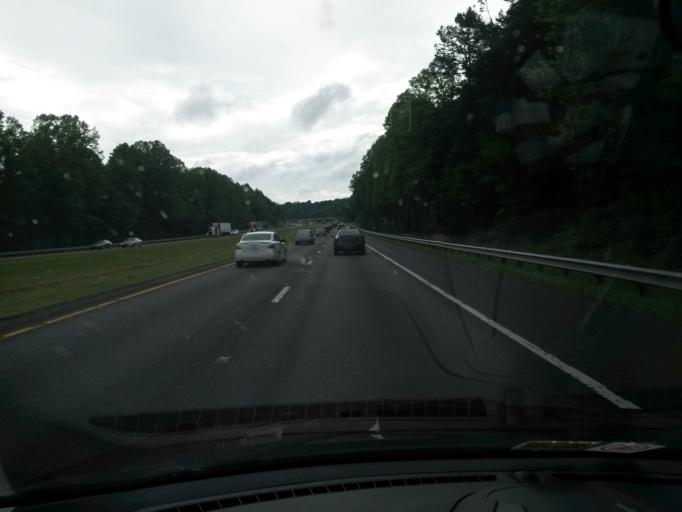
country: US
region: North Carolina
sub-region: Catawba County
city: Conover
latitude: 35.7059
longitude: -81.2709
